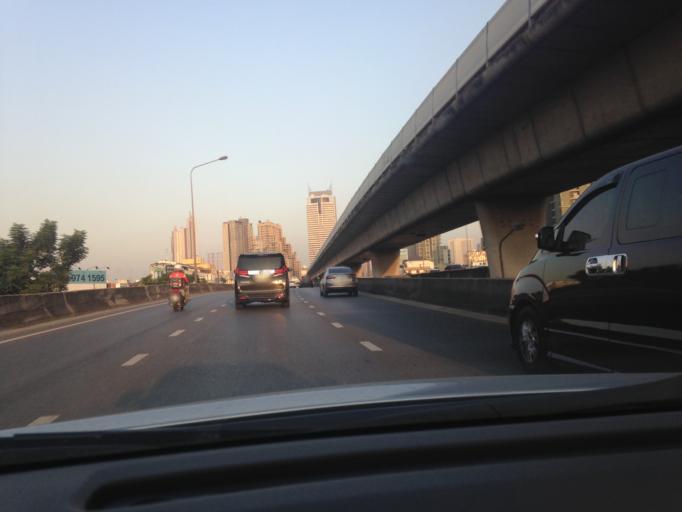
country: TH
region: Bangkok
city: Thon Buri
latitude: 13.7206
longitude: 100.4898
